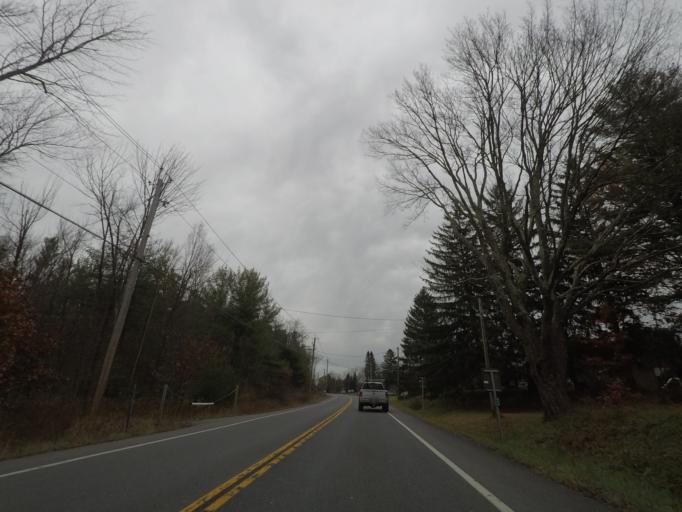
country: US
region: New York
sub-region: Albany County
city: Cohoes
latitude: 42.8192
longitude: -73.7546
